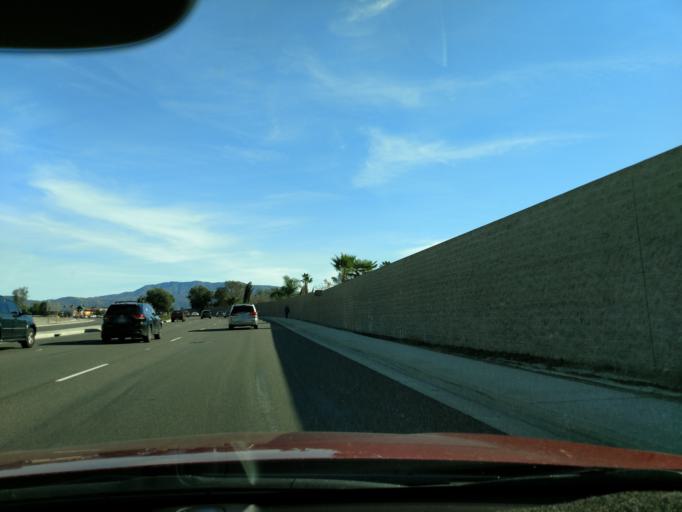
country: US
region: California
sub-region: Riverside County
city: Temecula
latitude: 33.4764
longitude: -117.1326
